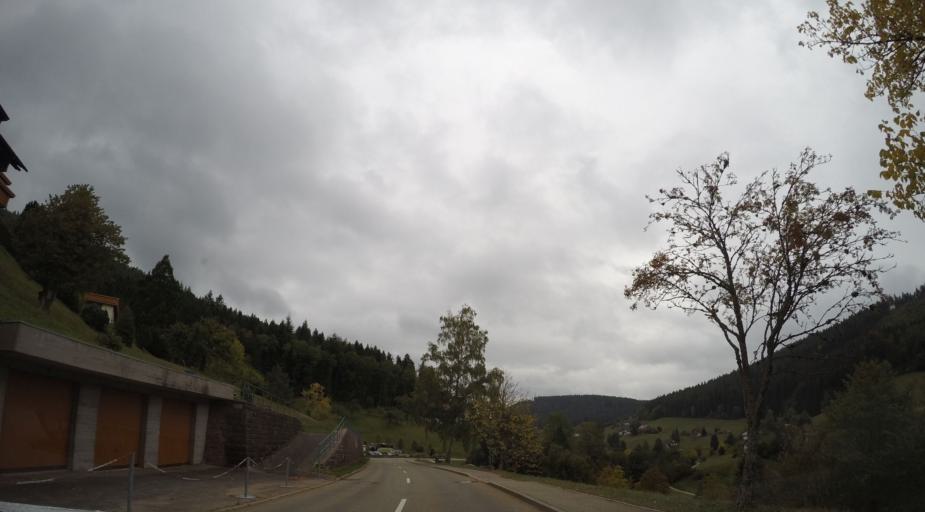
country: DE
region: Baden-Wuerttemberg
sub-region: Karlsruhe Region
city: Baiersbronn
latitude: 48.5342
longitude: 8.3605
